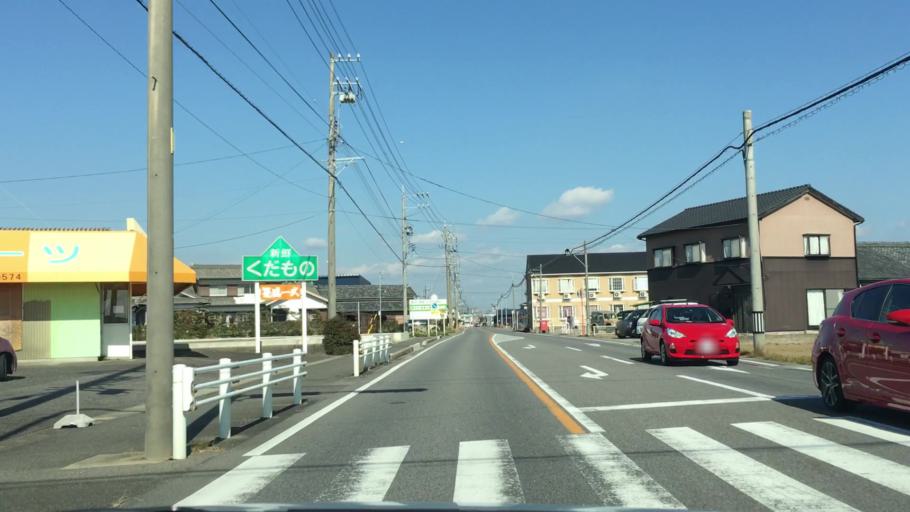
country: JP
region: Aichi
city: Anjo
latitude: 34.9992
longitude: 137.1154
